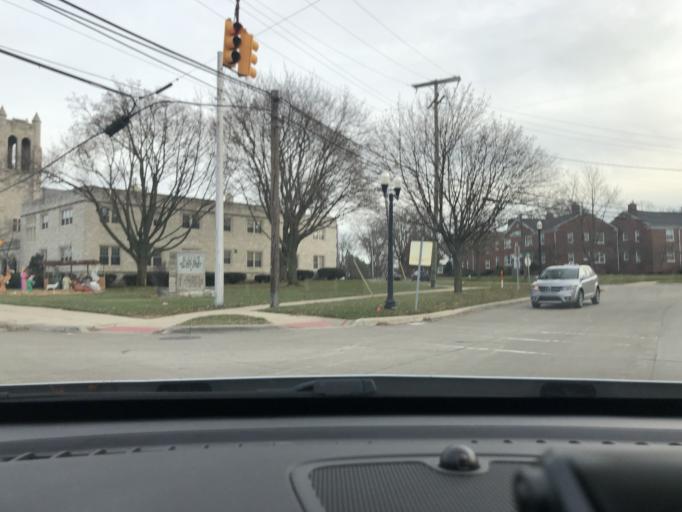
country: US
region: Michigan
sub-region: Wayne County
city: Dearborn Heights
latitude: 42.3024
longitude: -83.2424
